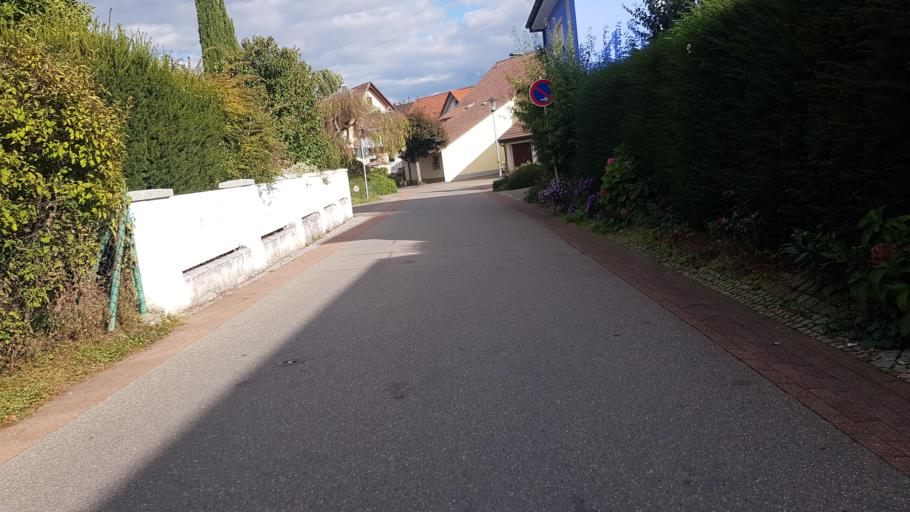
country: DE
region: Baden-Wuerttemberg
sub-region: Tuebingen Region
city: Immenstaad am Bodensee
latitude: 47.6622
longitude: 9.3604
